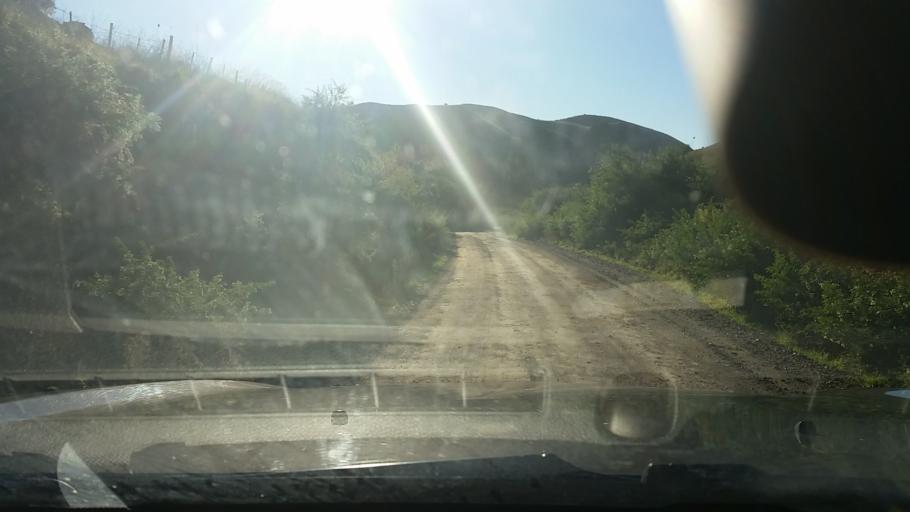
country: NZ
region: Marlborough
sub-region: Marlborough District
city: Blenheim
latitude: -41.5828
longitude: 174.0652
